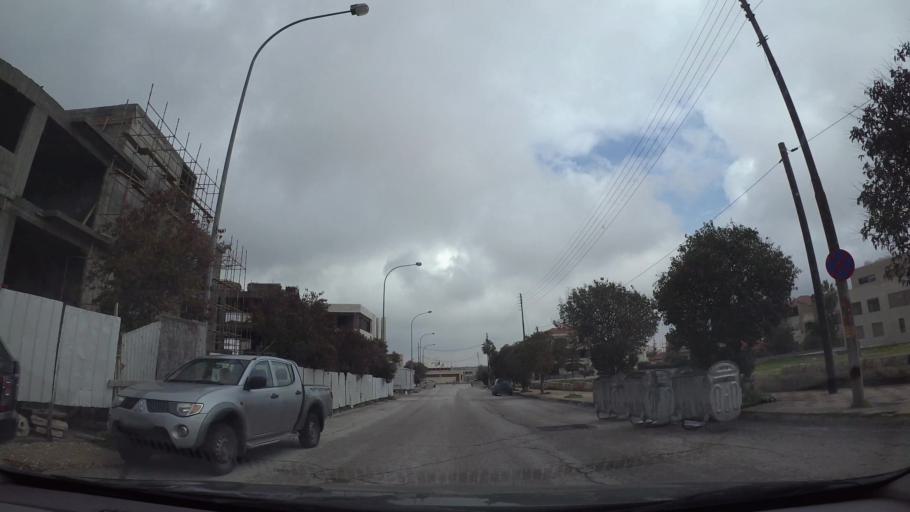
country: JO
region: Amman
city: Amman
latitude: 31.9483
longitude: 35.8942
